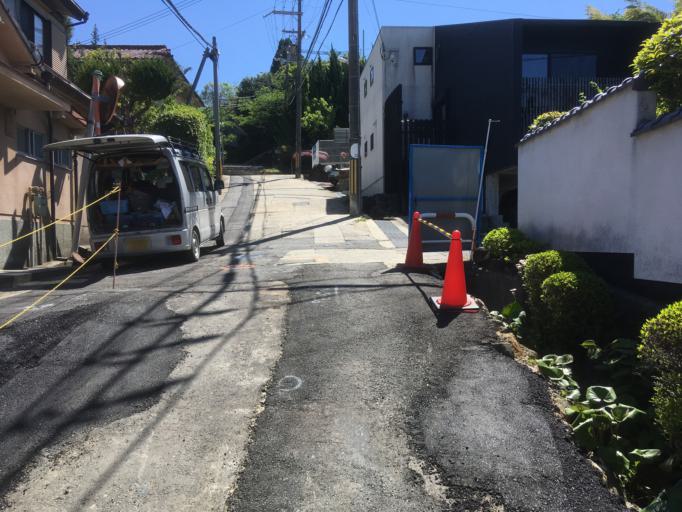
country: JP
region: Nara
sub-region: Ikoma-shi
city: Ikoma
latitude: 34.6873
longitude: 135.6926
